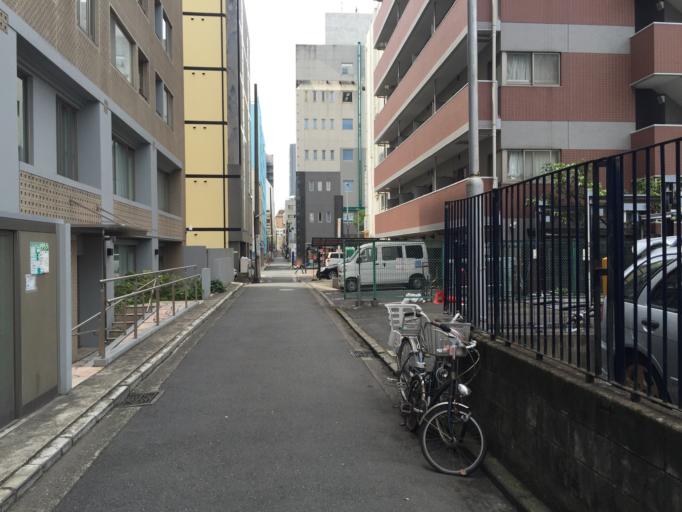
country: JP
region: Kanagawa
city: Yokohama
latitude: 35.4457
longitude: 139.6394
